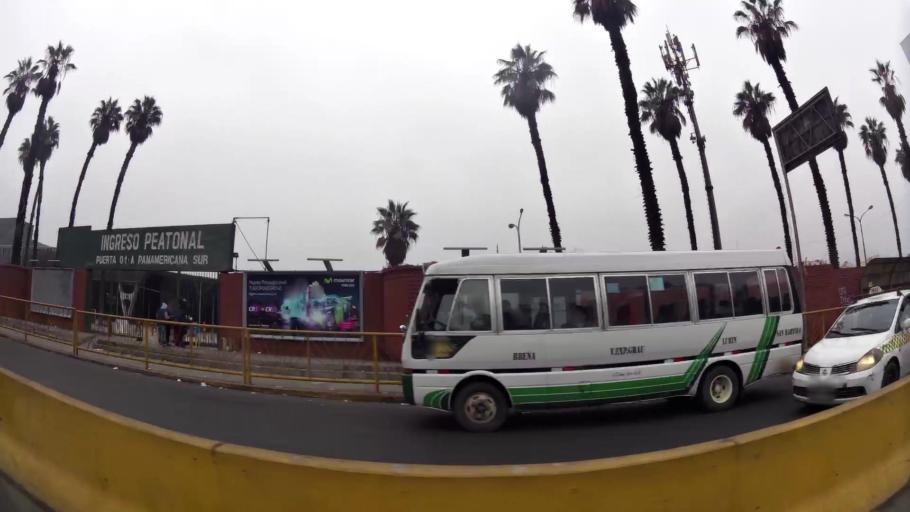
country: PE
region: Lima
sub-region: Lima
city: San Luis
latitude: -12.0928
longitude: -76.9805
